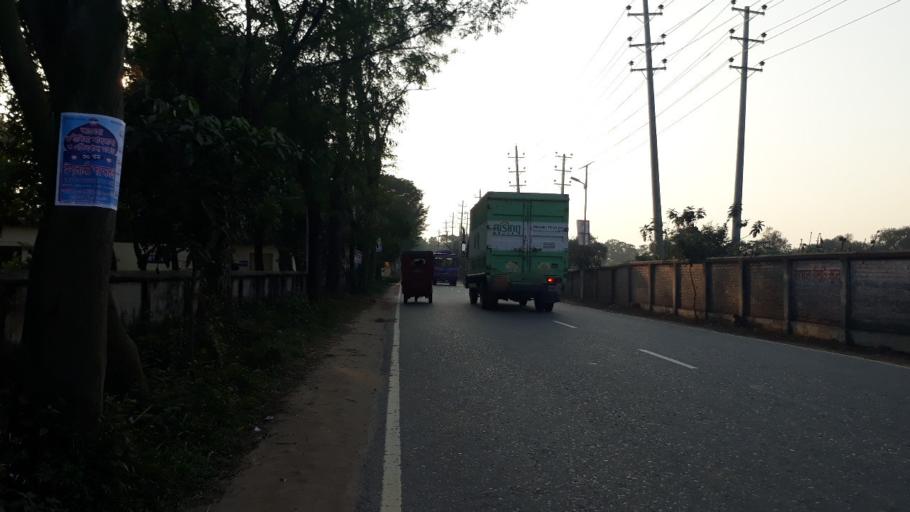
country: BD
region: Dhaka
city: Tungi
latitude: 23.8730
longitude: 90.2783
